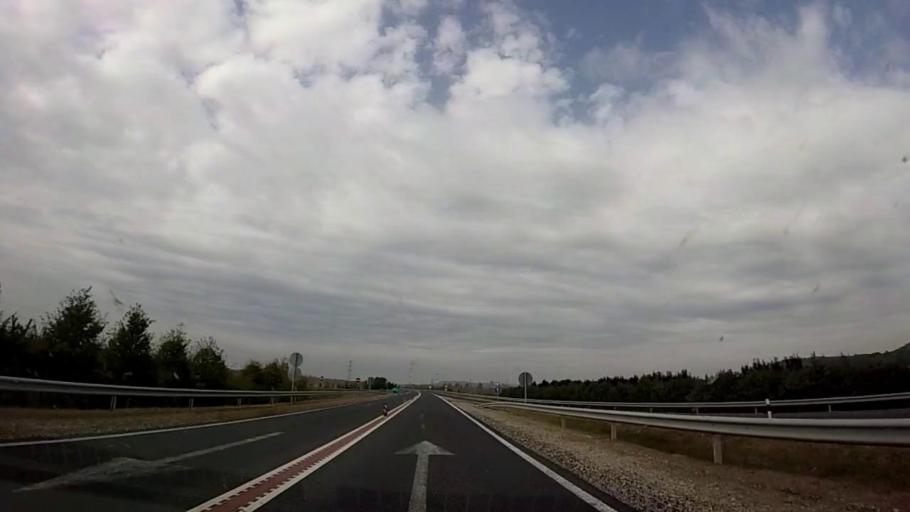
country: HR
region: Medimurska
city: Domasinec
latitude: 46.5030
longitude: 16.6082
